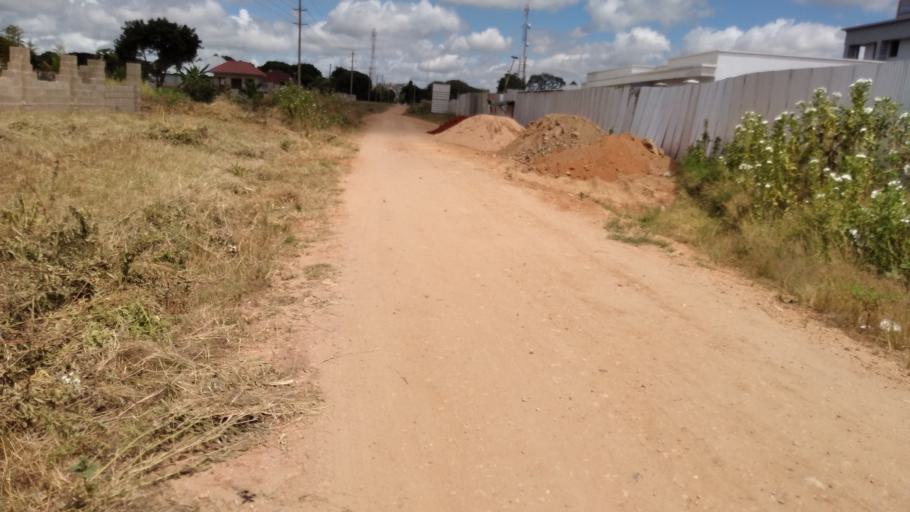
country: TZ
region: Dodoma
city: Dodoma
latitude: -6.1891
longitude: 35.7566
